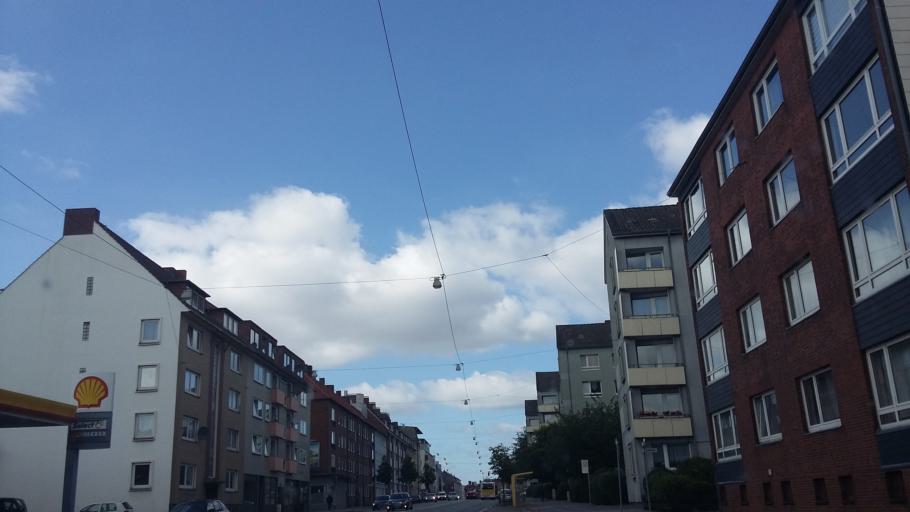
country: DE
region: Bremen
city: Bremerhaven
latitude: 53.5272
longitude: 8.5899
